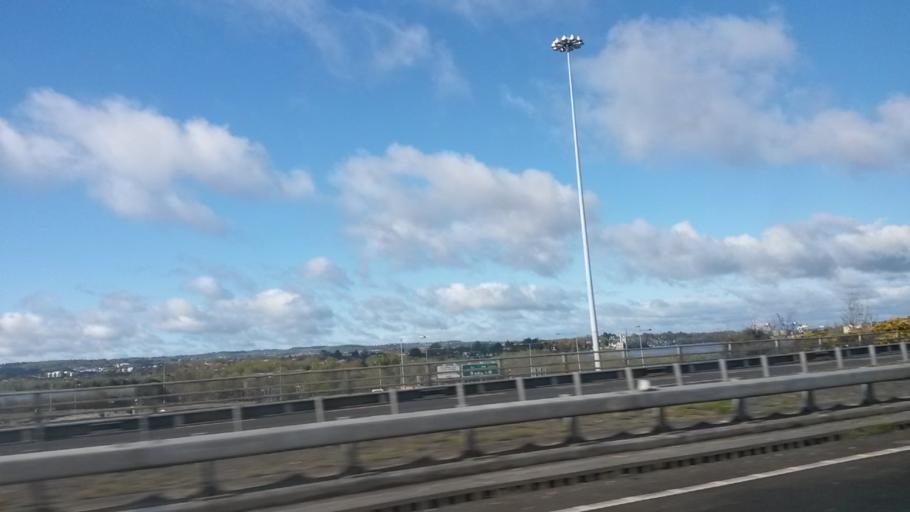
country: IE
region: Munster
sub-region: County Cork
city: Passage West
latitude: 51.9042
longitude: -8.3868
